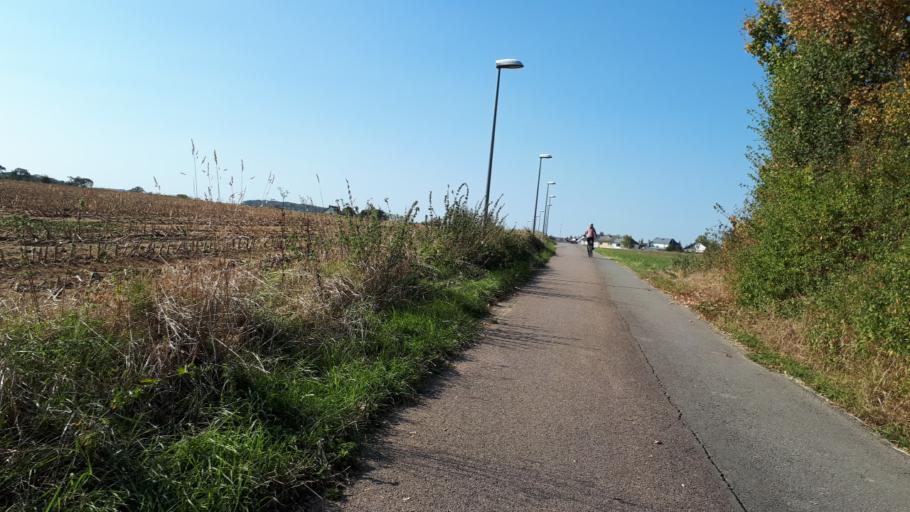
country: LU
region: Luxembourg
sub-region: Canton de Capellen
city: Mamer
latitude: 49.6209
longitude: 6.0331
